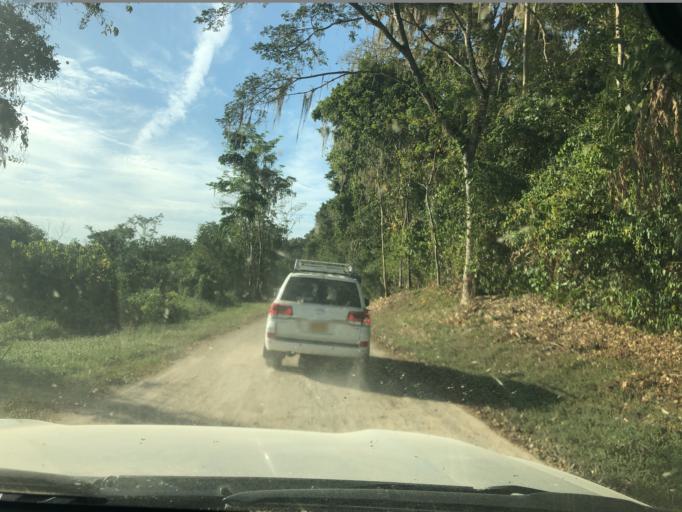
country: CR
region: Alajuela
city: San Jose
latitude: 11.1213
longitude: -85.2873
